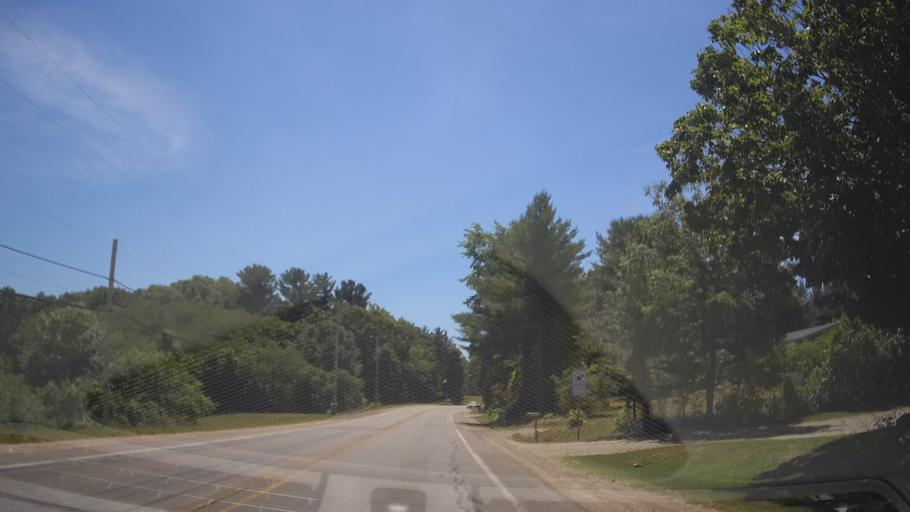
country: US
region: Michigan
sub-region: Grand Traverse County
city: Traverse City
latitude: 44.7156
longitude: -85.6856
